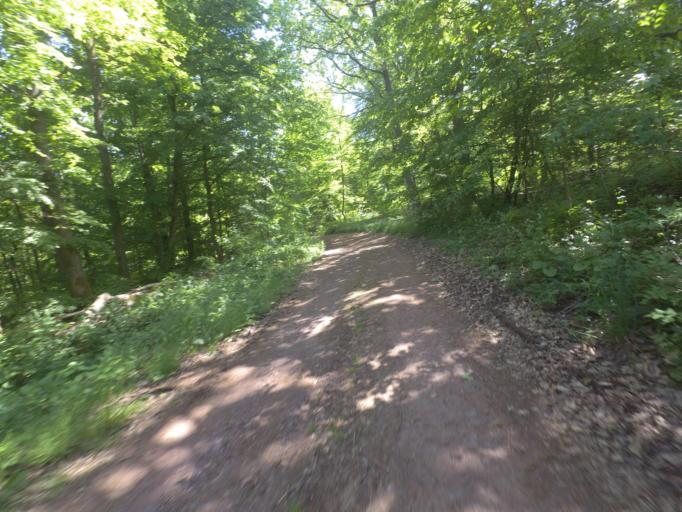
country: DE
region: Rheinland-Pfalz
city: Ruppertsecken
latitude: 49.6459
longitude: 7.9095
